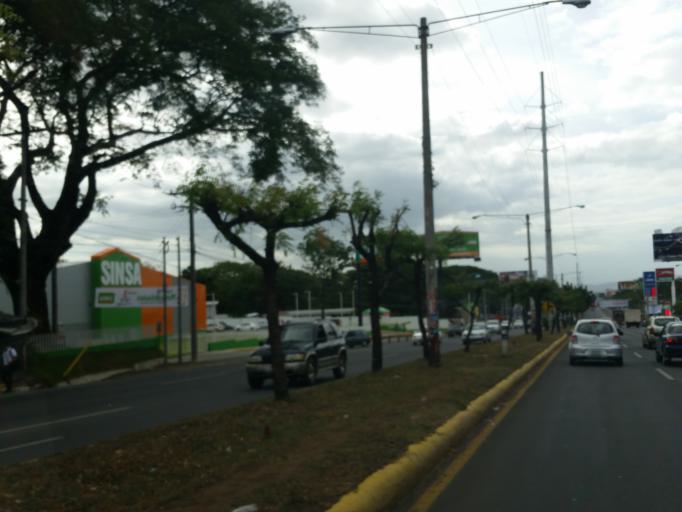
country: NI
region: Managua
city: Managua
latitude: 12.0961
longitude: -86.2396
